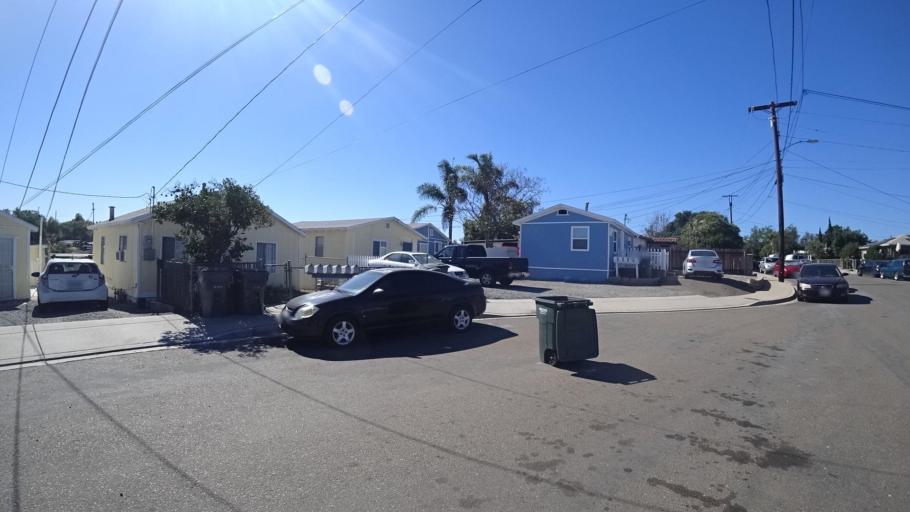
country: US
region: California
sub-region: San Diego County
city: Chula Vista
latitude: 32.6665
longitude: -117.0678
